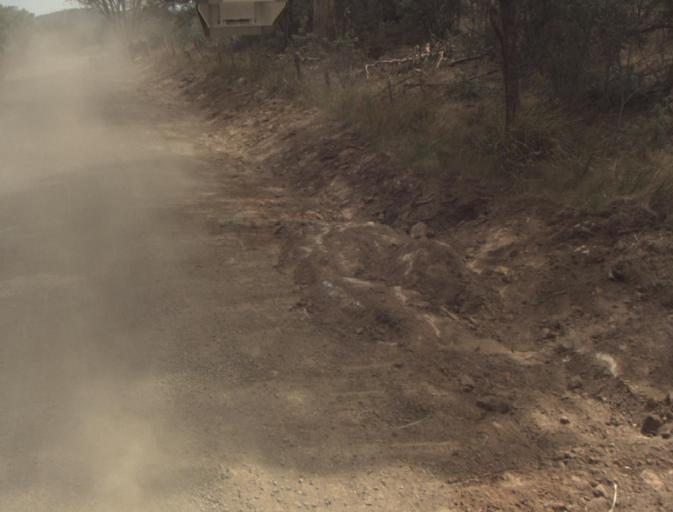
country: AU
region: Tasmania
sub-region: Northern Midlands
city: Evandale
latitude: -41.5120
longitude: 147.3472
